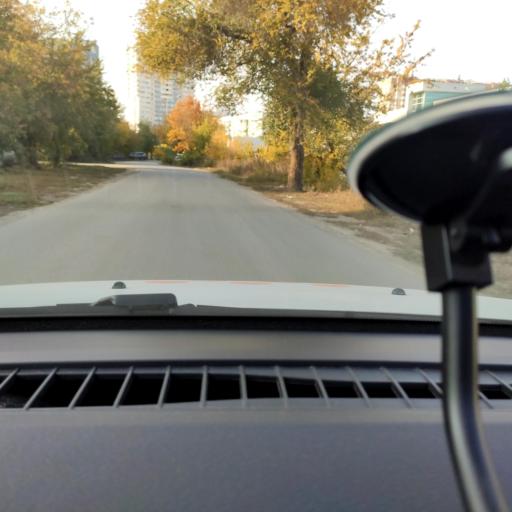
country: RU
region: Samara
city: Samara
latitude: 53.2499
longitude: 50.2132
